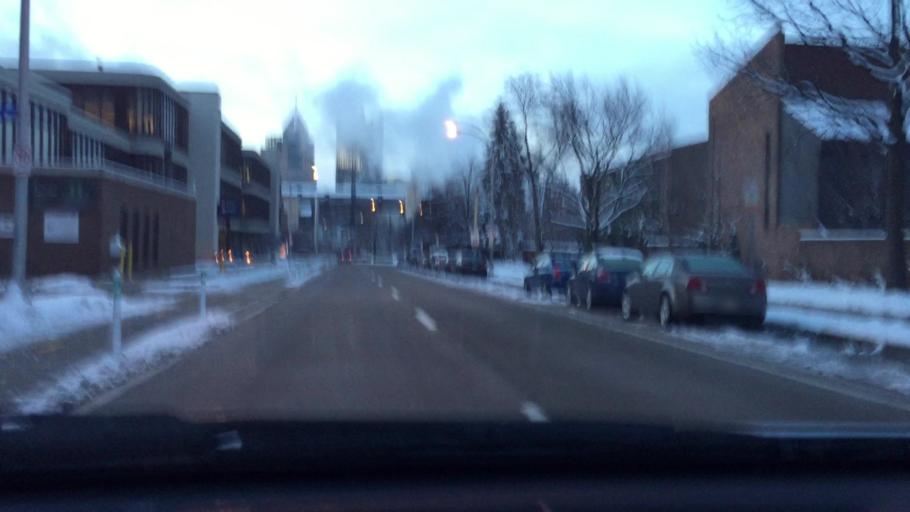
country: US
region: Pennsylvania
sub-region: Allegheny County
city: Pittsburgh
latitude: 40.4517
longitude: -80.0075
